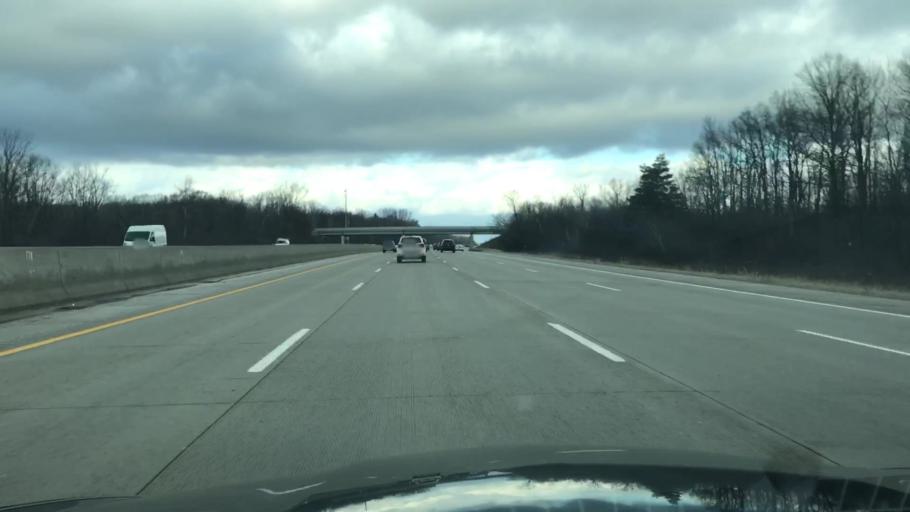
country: US
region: Michigan
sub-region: Saginaw County
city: Birch Run
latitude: 43.3044
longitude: -83.8323
